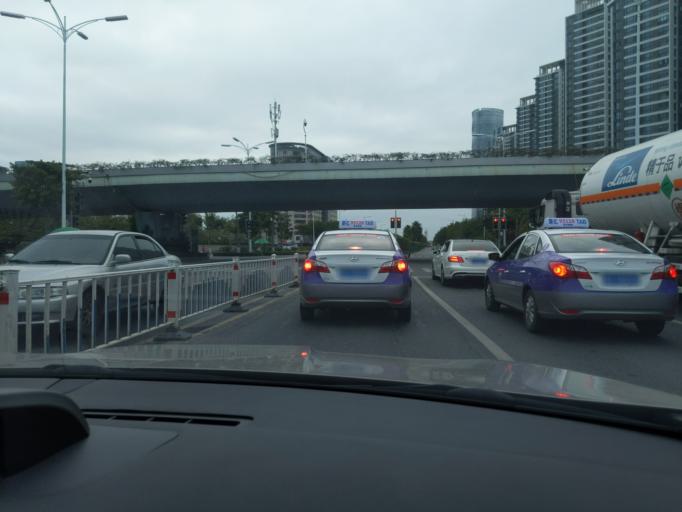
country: CN
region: Fujian
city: Liuwudian
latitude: 24.4830
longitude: 118.1811
